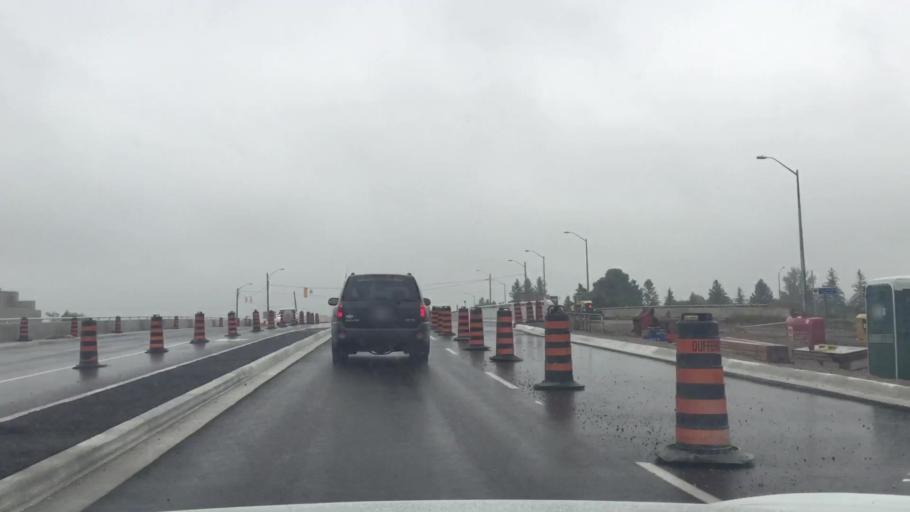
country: CA
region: Ontario
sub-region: Oxford County
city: Woodstock
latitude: 43.1092
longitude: -80.7357
